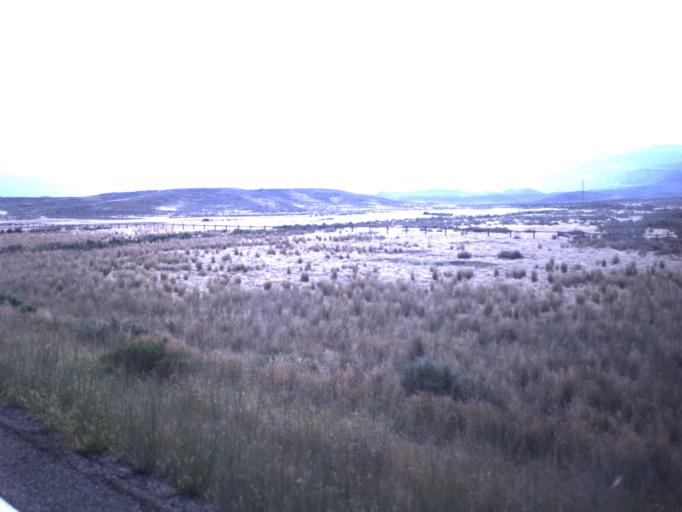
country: US
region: Utah
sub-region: Daggett County
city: Manila
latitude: 40.9836
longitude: -109.4438
